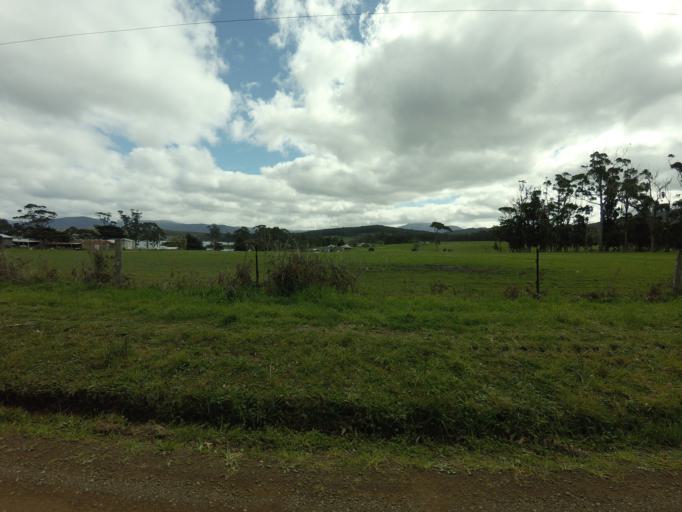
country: AU
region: Tasmania
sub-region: Huon Valley
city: Geeveston
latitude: -43.4357
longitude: 146.9862
